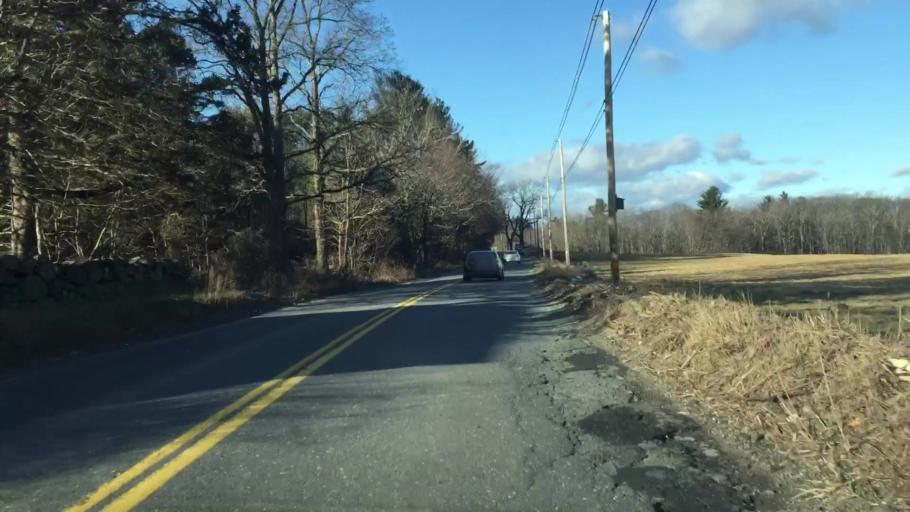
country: US
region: Massachusetts
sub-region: Worcester County
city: Sterling
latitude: 42.4186
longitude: -71.8050
